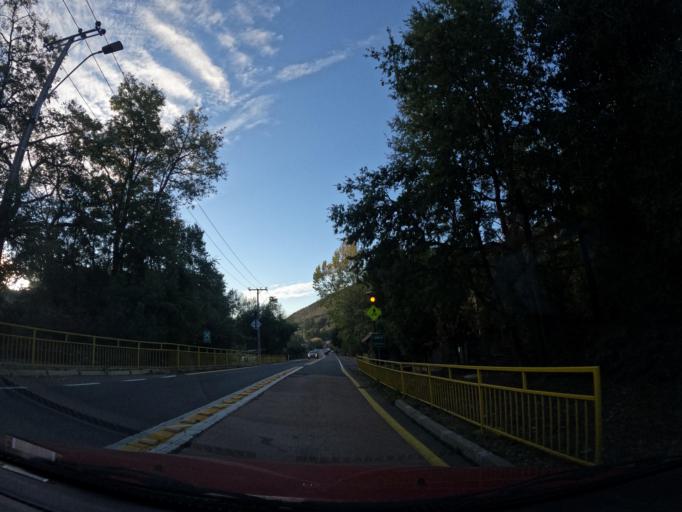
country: CL
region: Biobio
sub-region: Provincia de Nuble
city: Coihueco
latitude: -36.8559
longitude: -71.6440
